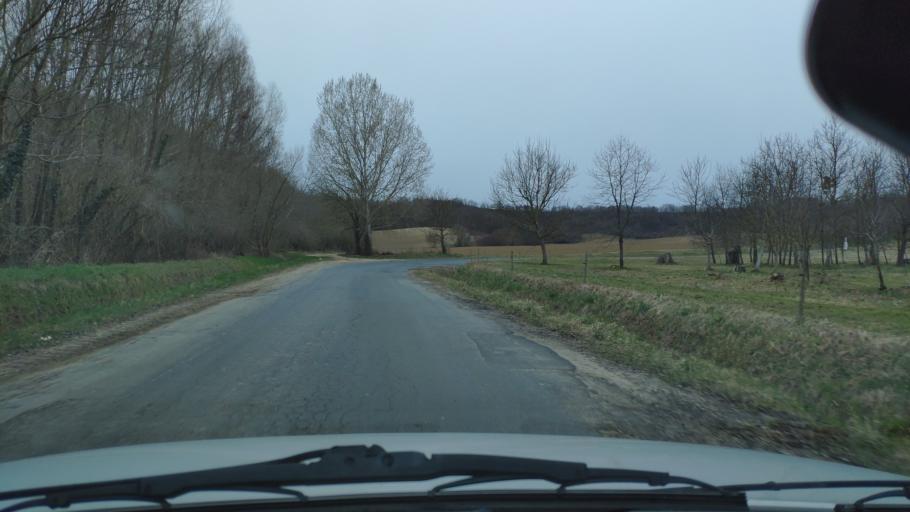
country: HU
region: Zala
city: Pacsa
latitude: 46.6847
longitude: 17.0504
